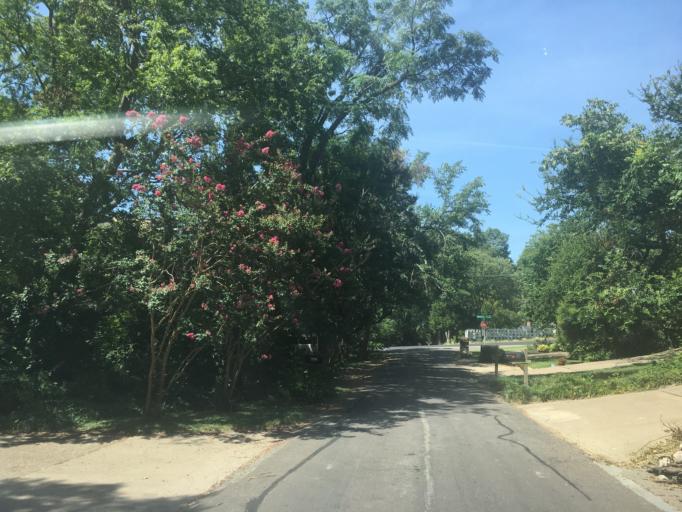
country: US
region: Texas
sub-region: Dallas County
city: Highland Park
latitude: 32.8673
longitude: -96.7244
